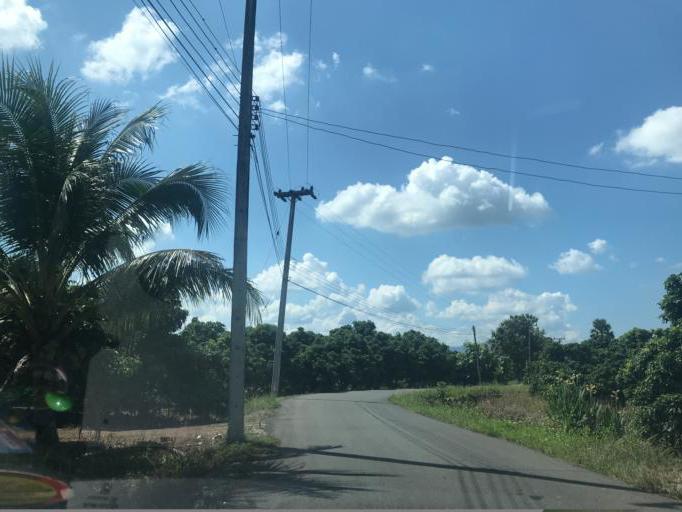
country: TH
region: Chiang Mai
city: Mae Wang
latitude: 18.5654
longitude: 98.8357
